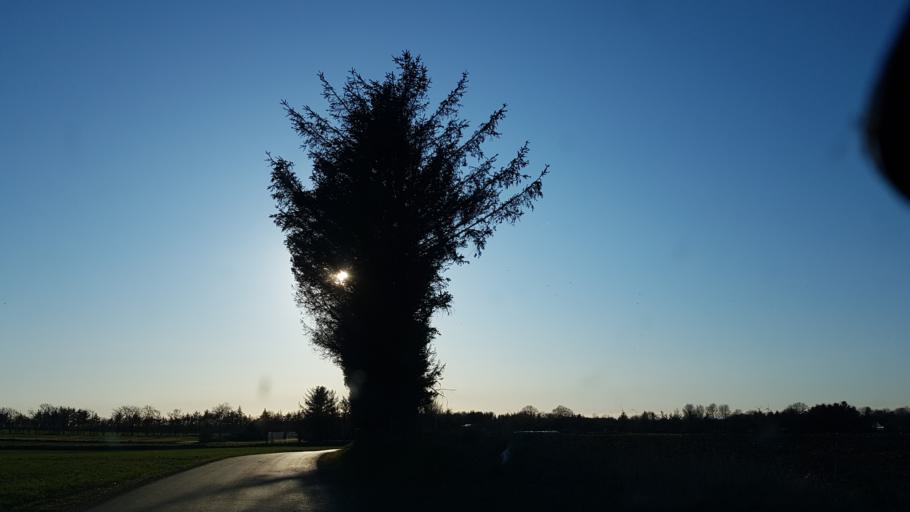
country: DK
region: South Denmark
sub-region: Esbjerg Kommune
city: Bramming
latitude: 55.4213
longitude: 8.6529
